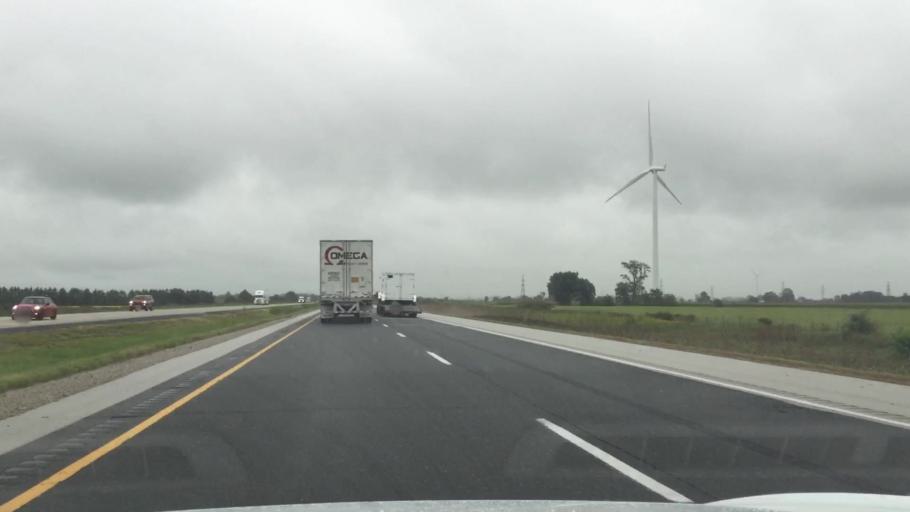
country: CA
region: Ontario
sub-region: Lambton County
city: Walpole Island
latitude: 42.3279
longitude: -82.2337
